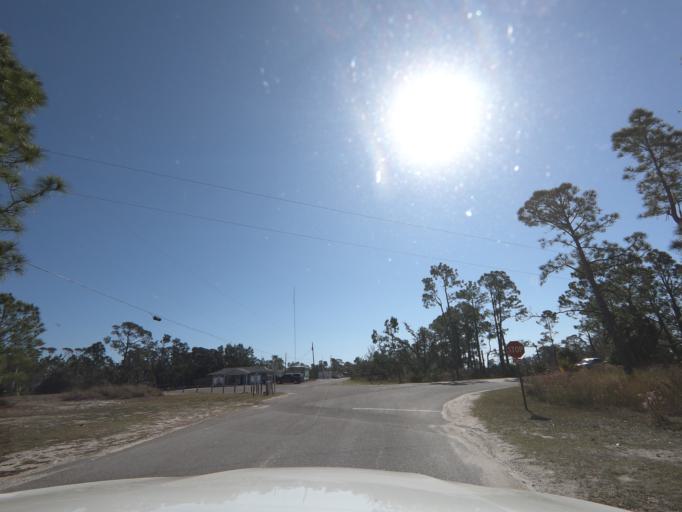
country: US
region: Florida
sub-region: Bay County
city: Lower Grand Lagoon
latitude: 30.1313
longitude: -85.7328
